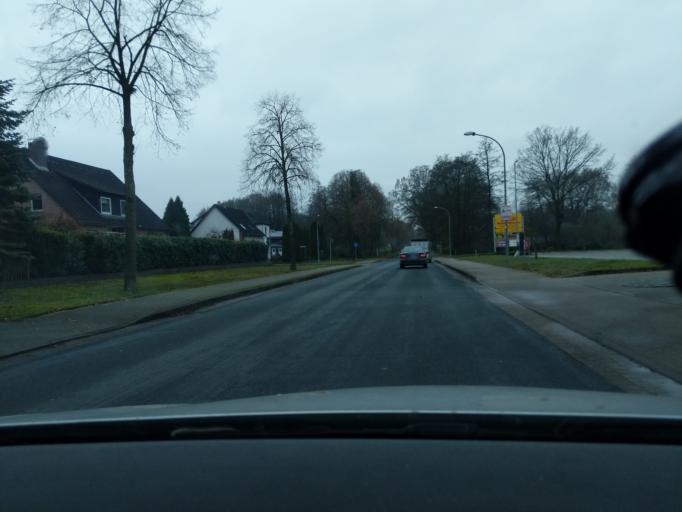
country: DE
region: Lower Saxony
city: Heeslingen
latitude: 53.3114
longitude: 9.3295
